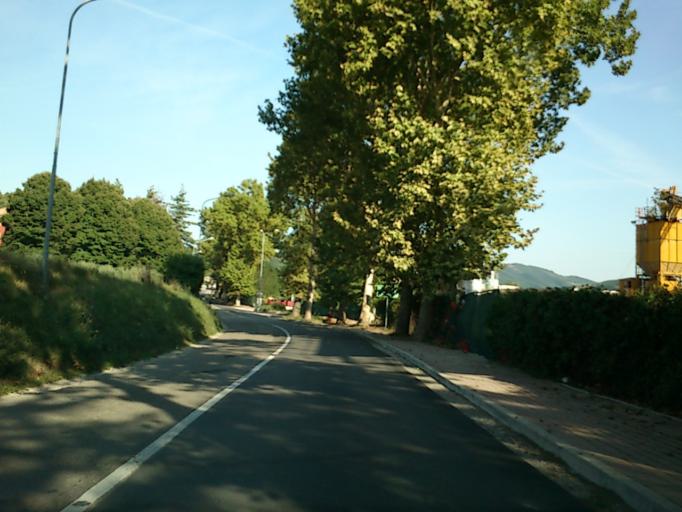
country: IT
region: The Marches
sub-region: Provincia di Pesaro e Urbino
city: Canavaccio
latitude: 43.6780
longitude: 12.7472
